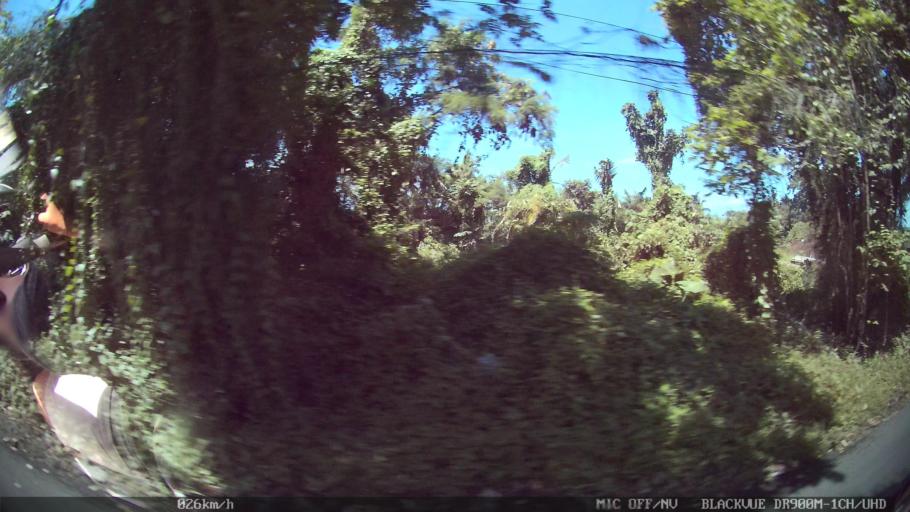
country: ID
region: Bali
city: Banjar Kelodan
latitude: -8.5400
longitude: 115.3351
